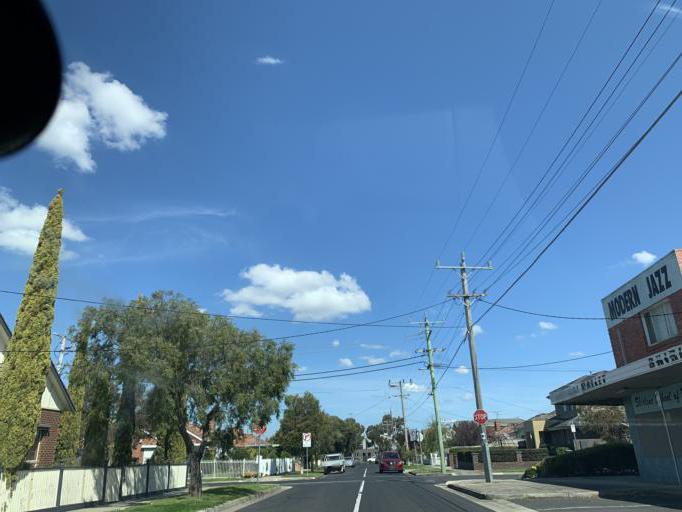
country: AU
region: Victoria
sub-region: Moreland
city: Pascoe Vale
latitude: -37.7364
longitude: 144.9349
